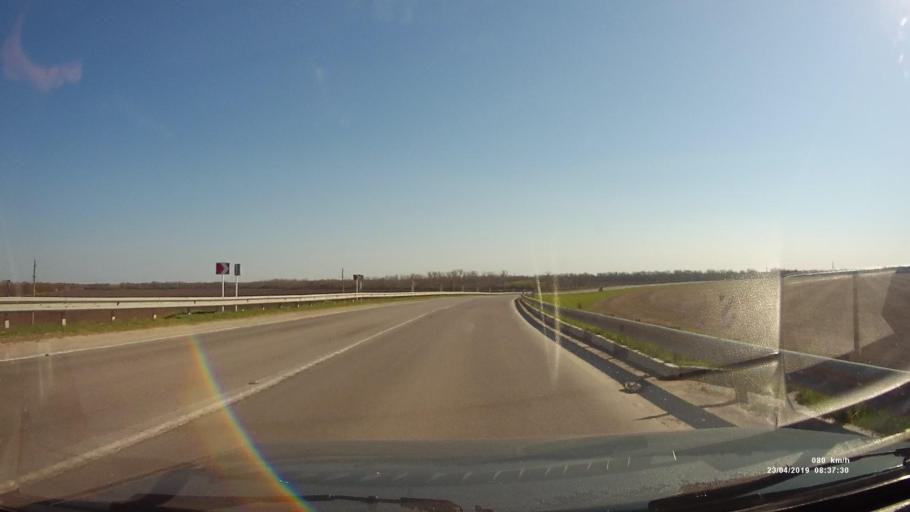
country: RU
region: Rostov
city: Tselina
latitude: 46.5309
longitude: 41.1711
